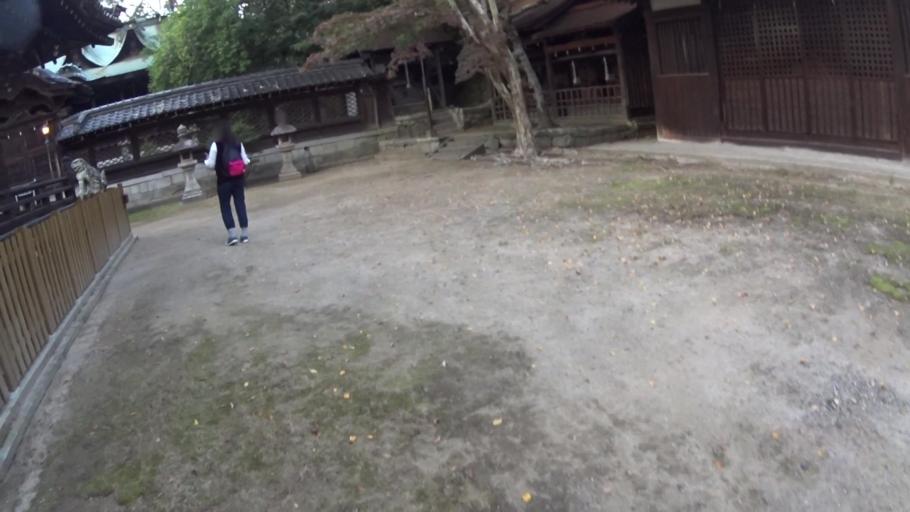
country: JP
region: Osaka
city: Ikeda
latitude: 34.8299
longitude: 135.4253
